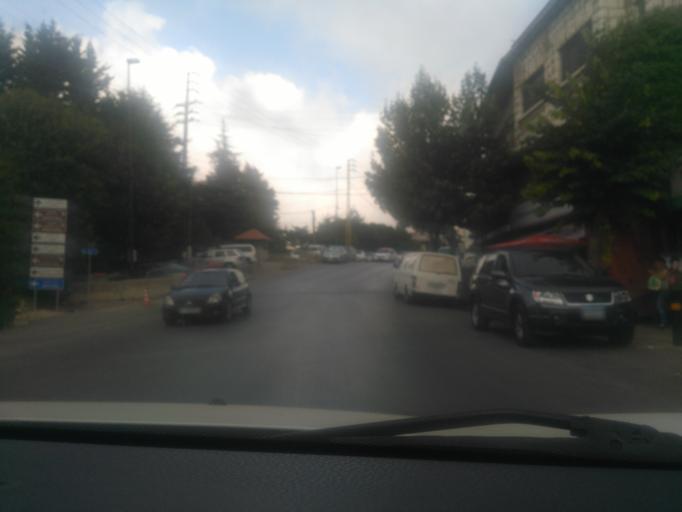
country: LB
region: Mont-Liban
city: Djounie
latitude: 33.9226
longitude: 35.6850
